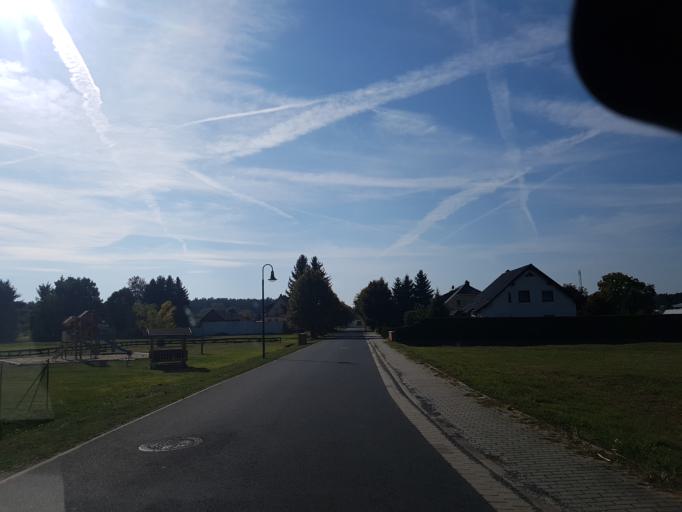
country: DE
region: Brandenburg
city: Hohenbucko
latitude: 51.7644
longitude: 13.4695
